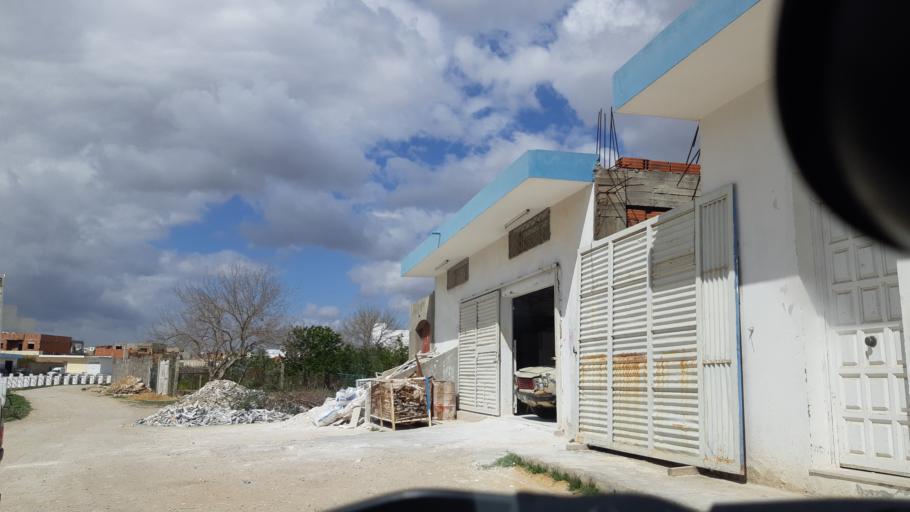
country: TN
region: Susah
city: Akouda
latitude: 35.8719
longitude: 10.5457
